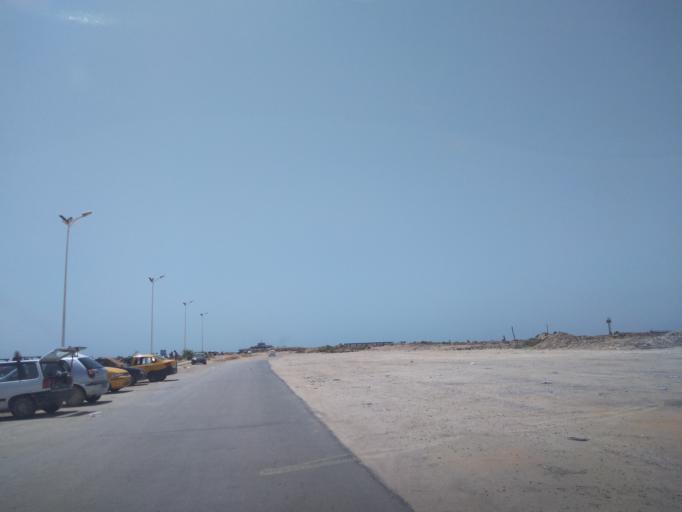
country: TN
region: Safaqis
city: Al Qarmadah
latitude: 34.7268
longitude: 10.7817
